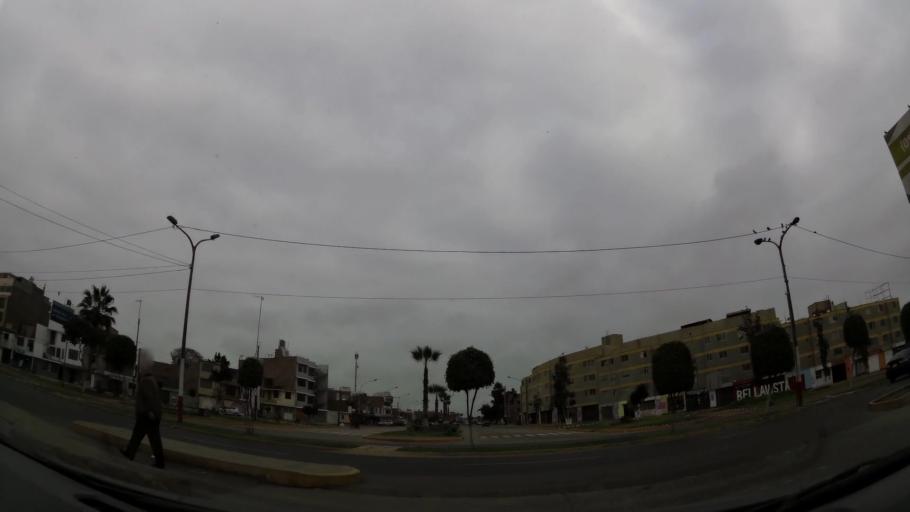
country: PE
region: Callao
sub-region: Callao
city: Callao
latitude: -12.0553
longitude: -77.1078
